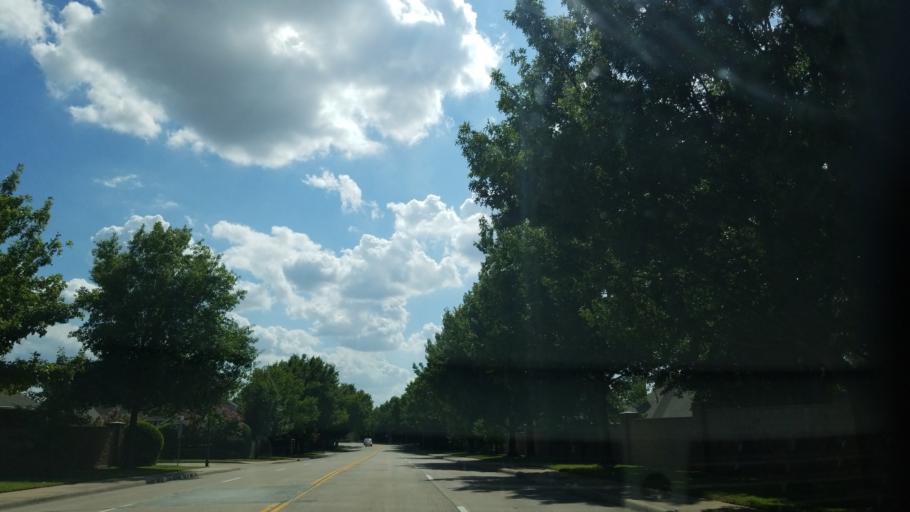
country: US
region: Texas
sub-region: Tarrant County
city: Bedford
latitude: 32.8471
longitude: -97.1181
